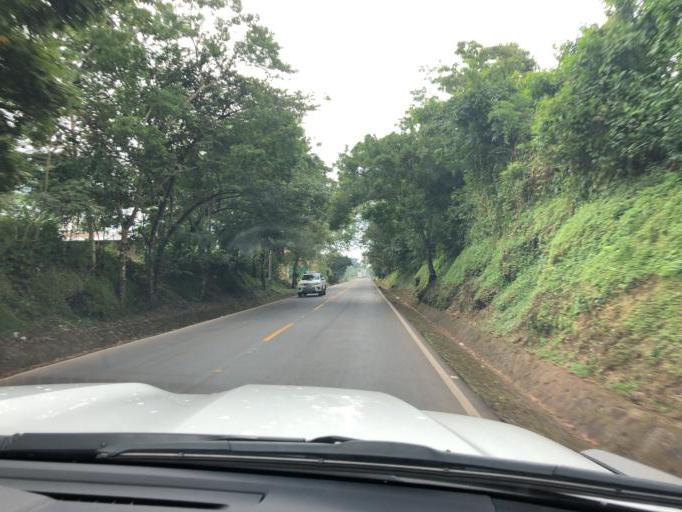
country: NI
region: Chontales
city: Villa Sandino
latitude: 11.9966
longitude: -84.7871
